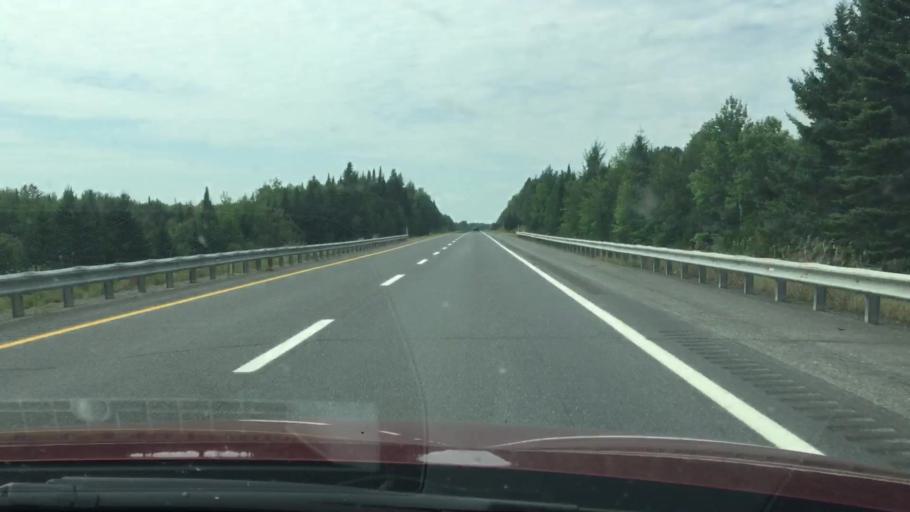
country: US
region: Maine
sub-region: Aroostook County
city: Hodgdon
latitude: 46.1409
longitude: -67.9962
